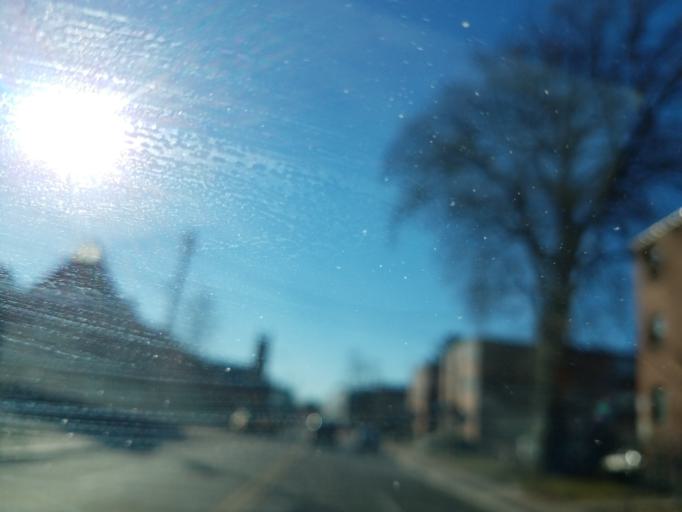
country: US
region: Connecticut
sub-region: Hartford County
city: Hartford
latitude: 41.7716
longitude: -72.6933
